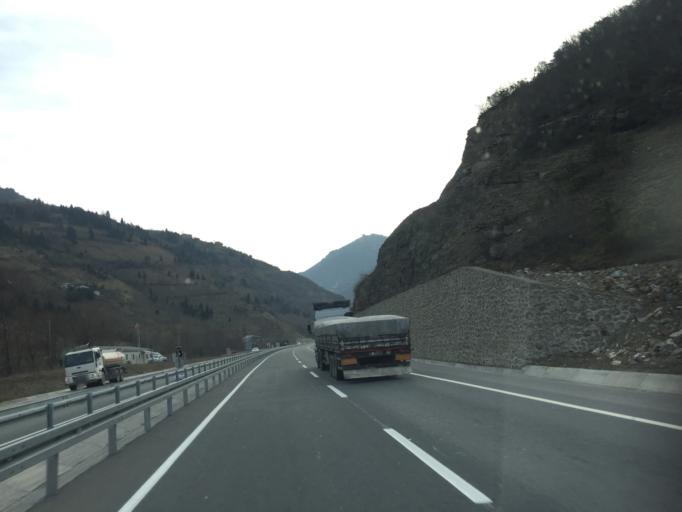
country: TR
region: Trabzon
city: Macka
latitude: 40.7908
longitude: 39.5805
